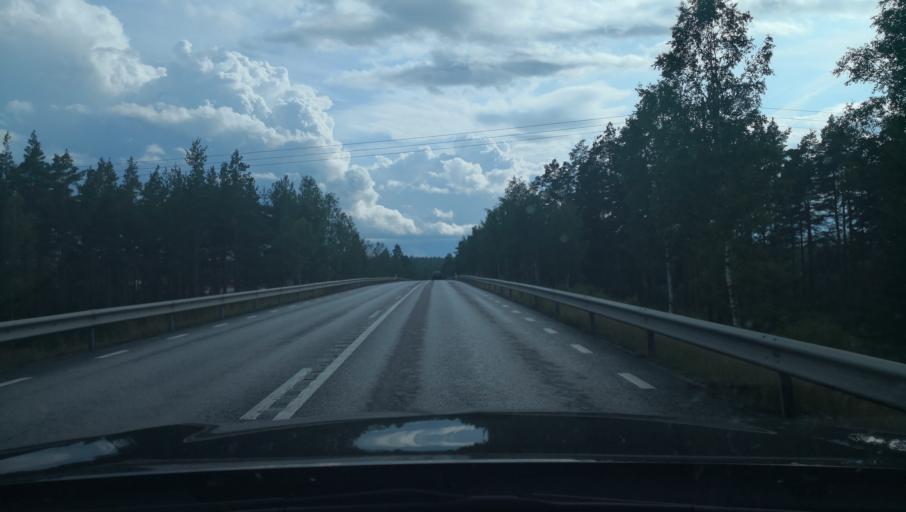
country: SE
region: Kalmar
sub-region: Hultsfreds Kommun
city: Hultsfred
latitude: 57.5055
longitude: 15.8283
